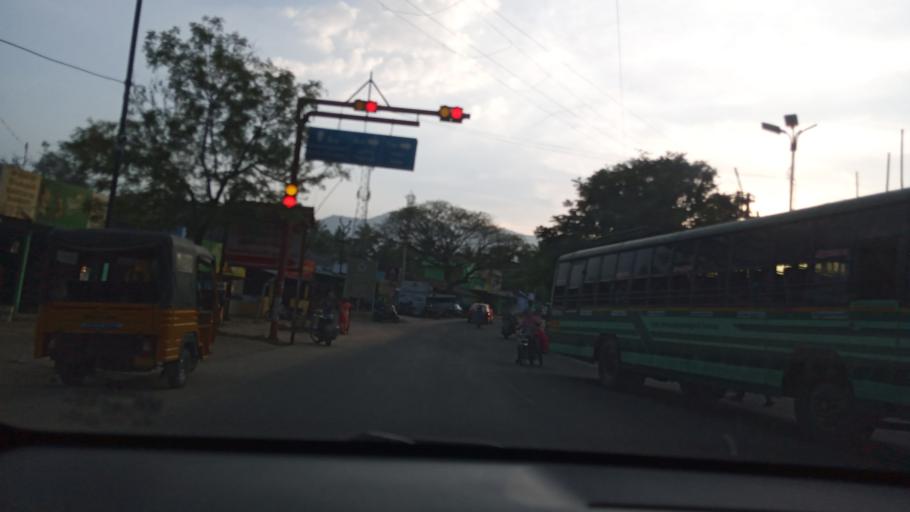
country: IN
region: Tamil Nadu
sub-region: Coimbatore
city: Perur
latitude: 10.9448
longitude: 76.7705
